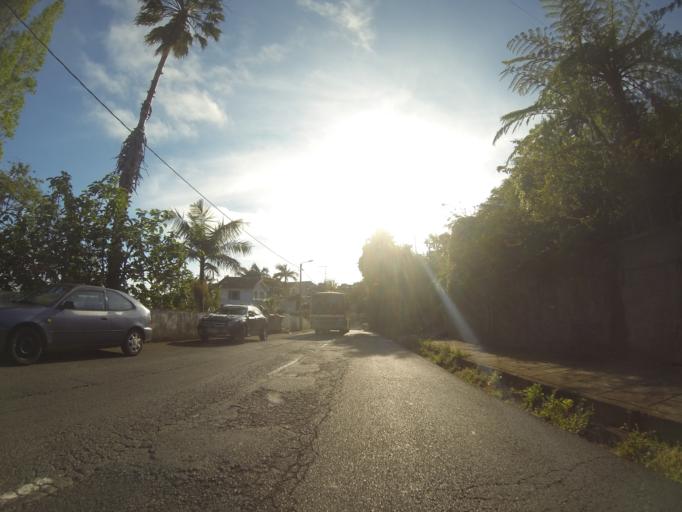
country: PT
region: Madeira
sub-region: Funchal
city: Nossa Senhora do Monte
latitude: 32.6613
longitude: -16.8757
